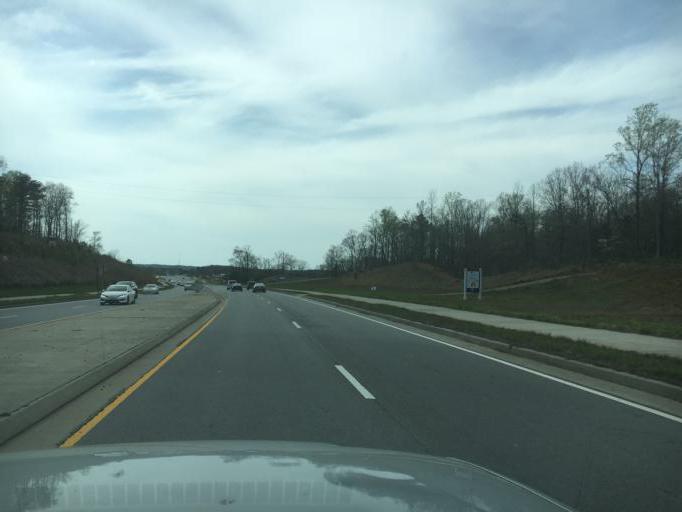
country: US
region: Georgia
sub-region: Hall County
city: Flowery Branch
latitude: 34.1101
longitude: -83.8666
